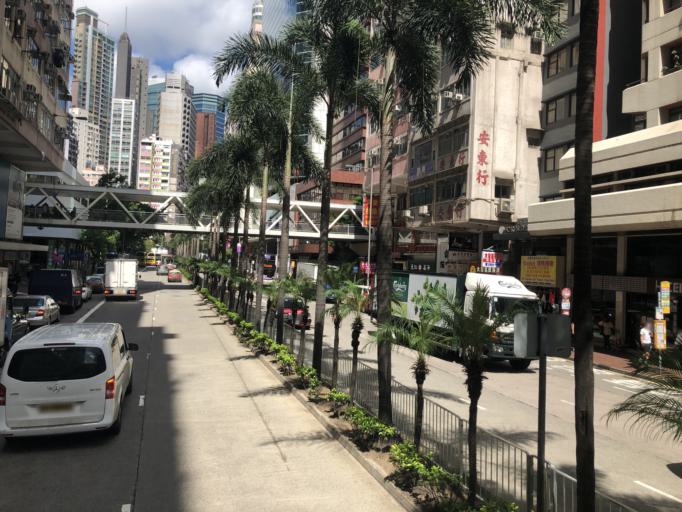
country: HK
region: Wanchai
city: Wan Chai
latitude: 22.2776
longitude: 114.1738
